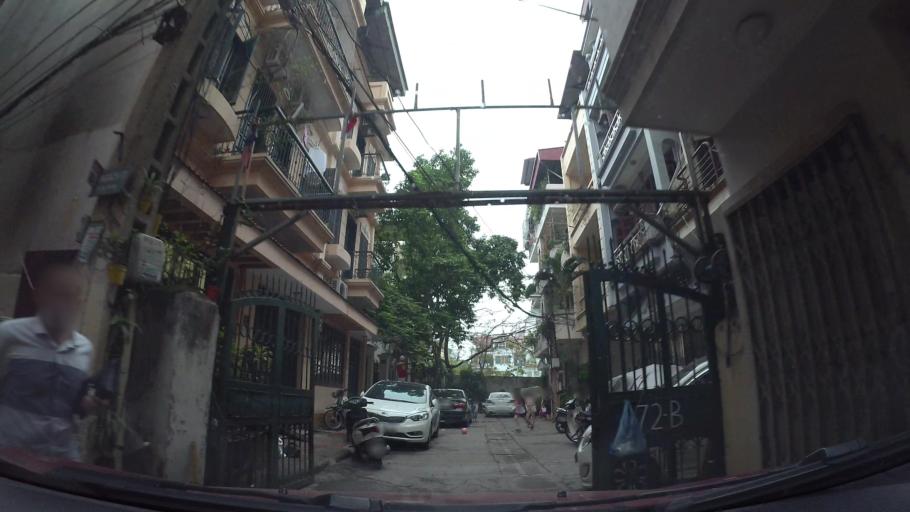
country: VN
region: Ha Noi
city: Hanoi
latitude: 21.0254
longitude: 105.8356
